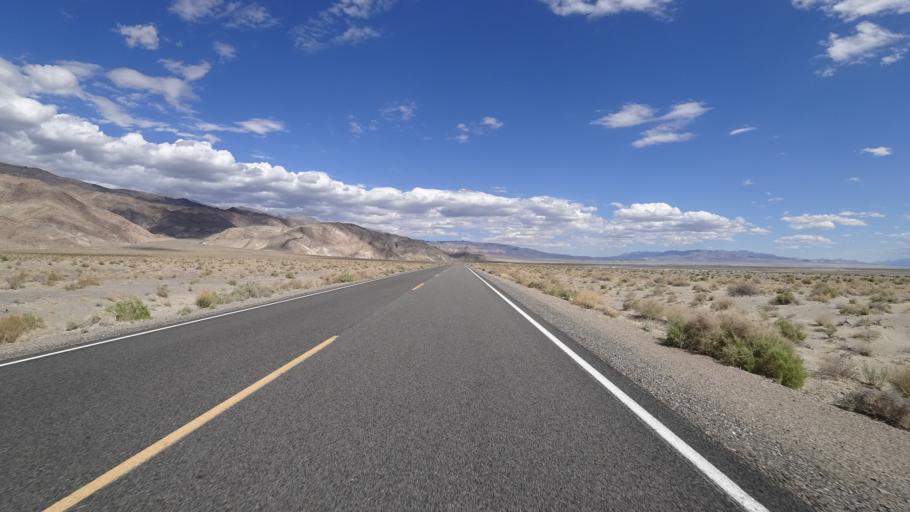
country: US
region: California
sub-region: Inyo County
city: Lone Pine
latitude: 36.5498
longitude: -117.9487
